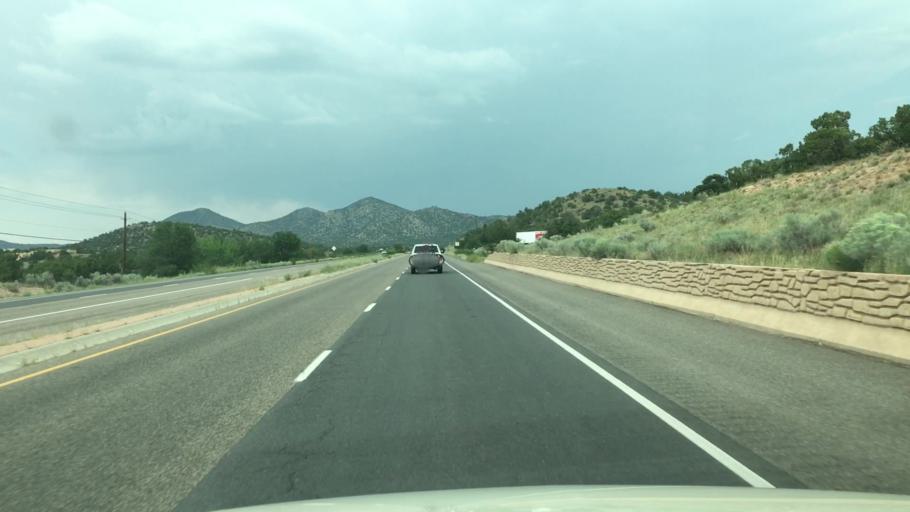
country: US
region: New Mexico
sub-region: Santa Fe County
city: Eldorado at Santa Fe
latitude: 35.5418
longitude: -105.8849
